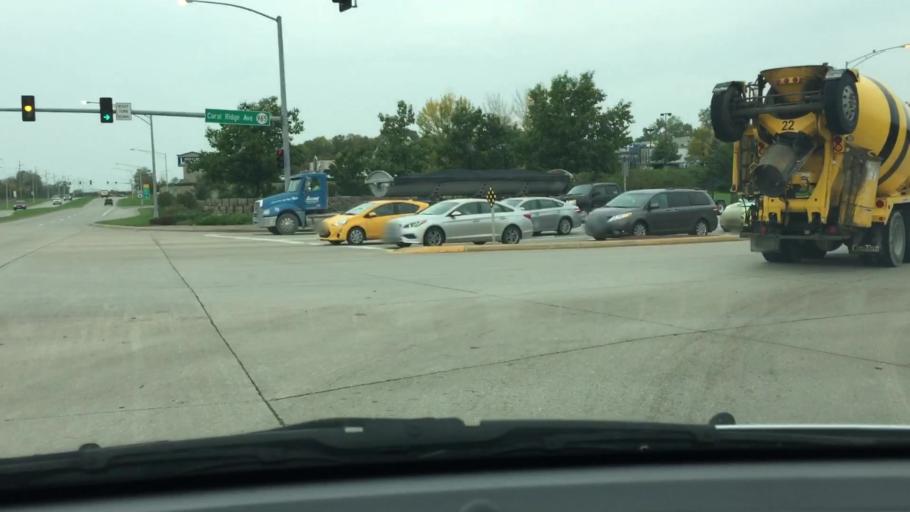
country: US
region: Iowa
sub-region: Johnson County
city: Coralville
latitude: 41.6886
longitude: -91.6086
